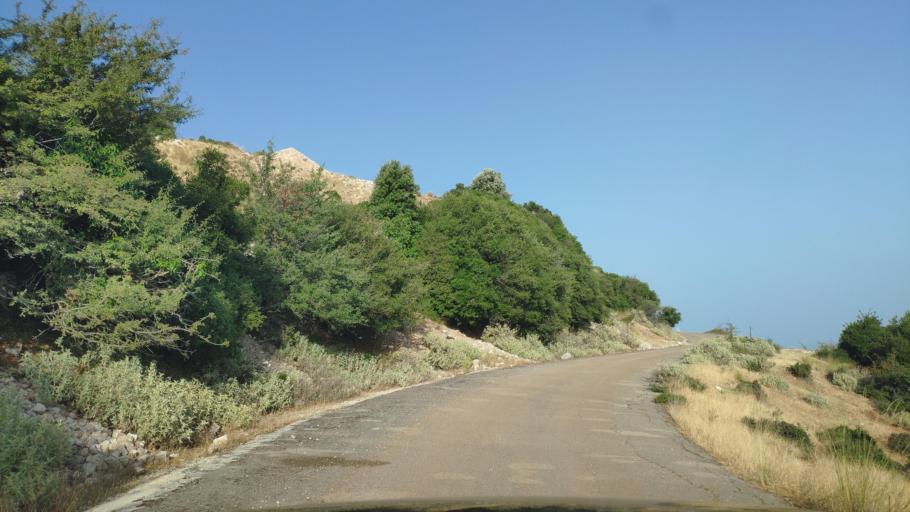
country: GR
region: West Greece
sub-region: Nomos Aitolias kai Akarnanias
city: Monastirakion
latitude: 38.8397
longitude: 20.9749
